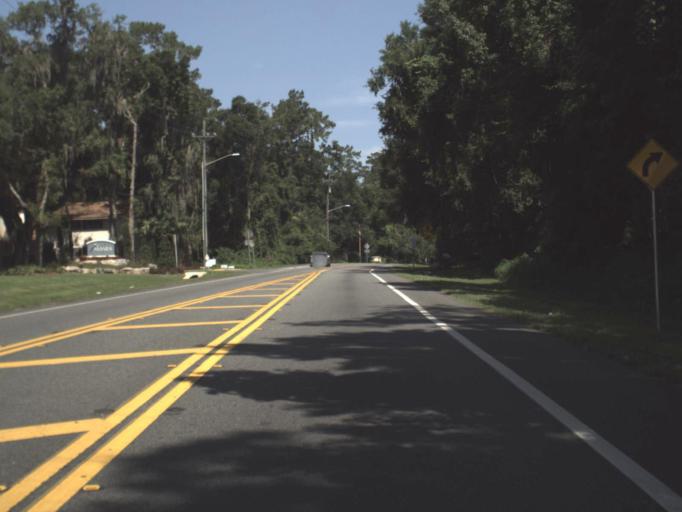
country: US
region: Florida
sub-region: Alachua County
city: Gainesville
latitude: 29.6301
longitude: -82.3235
